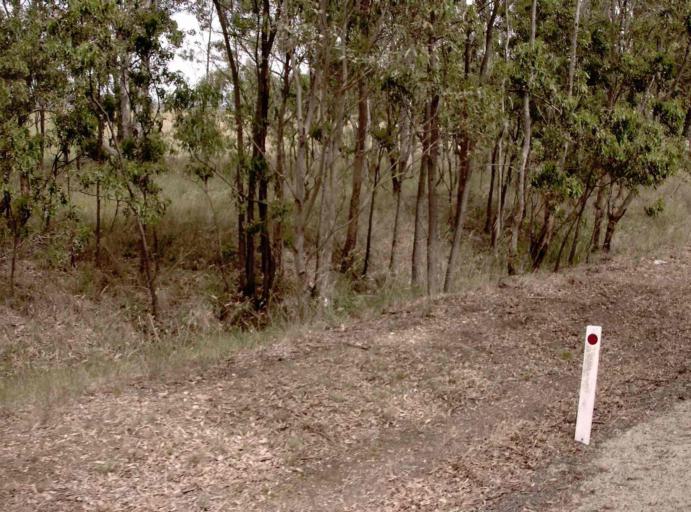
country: AU
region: Victoria
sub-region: Wellington
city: Sale
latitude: -37.9044
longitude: 147.0764
